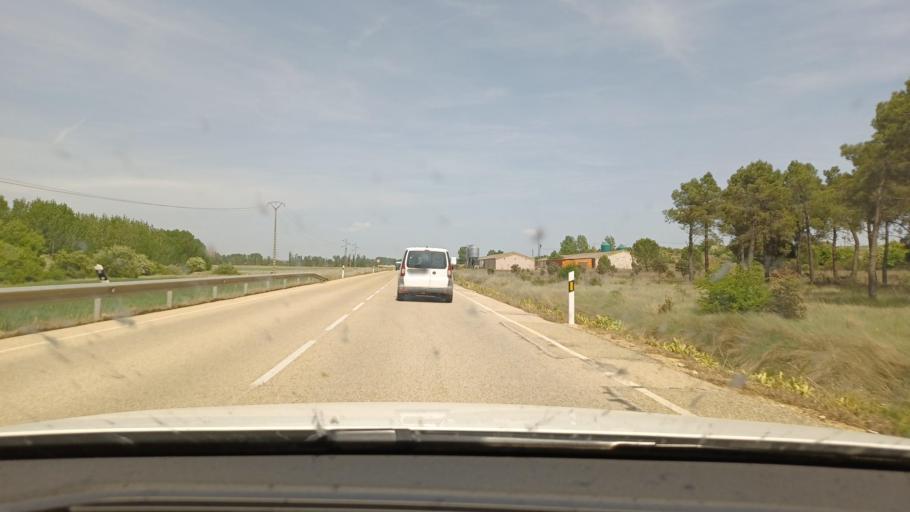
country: ES
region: Castille and Leon
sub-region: Provincia de Soria
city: Barca
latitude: 41.4701
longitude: -2.5795
